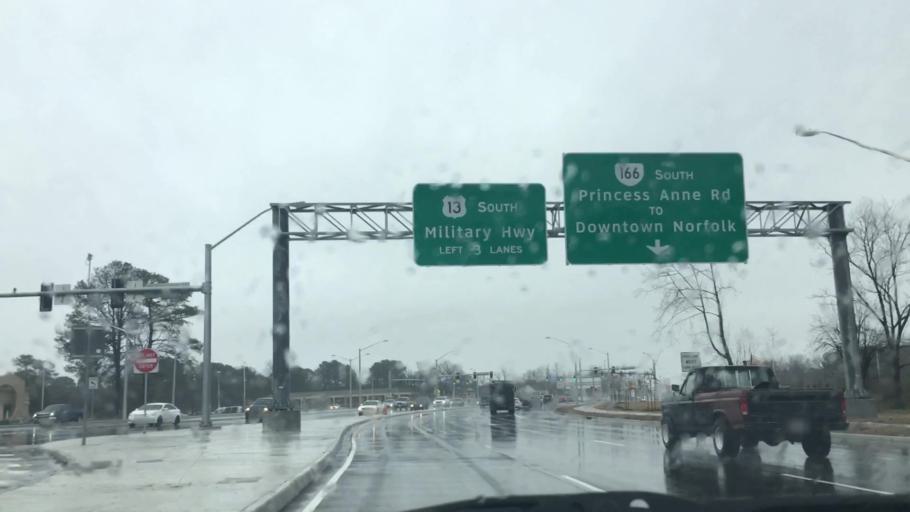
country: US
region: Virginia
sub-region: City of Norfolk
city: Norfolk
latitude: 36.8766
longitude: -76.2111
